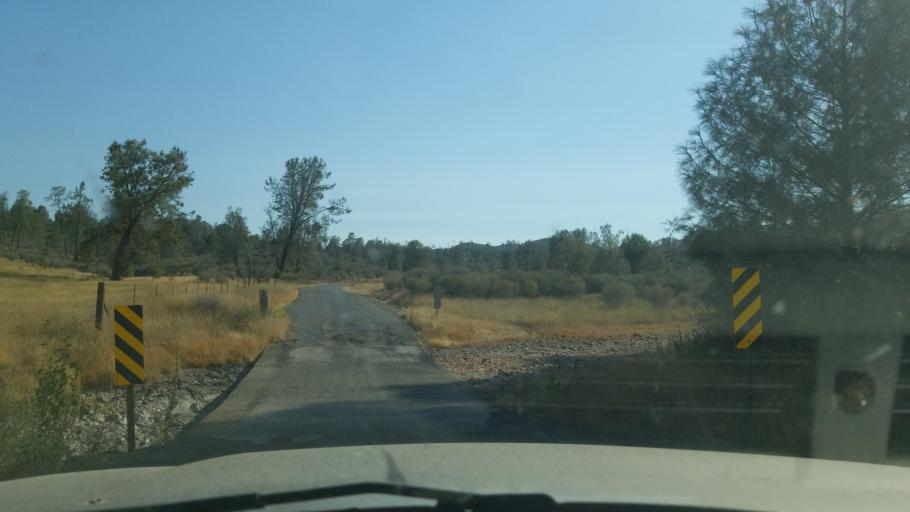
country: US
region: California
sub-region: Tuolumne County
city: Jamestown
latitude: 37.8494
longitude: -120.4581
